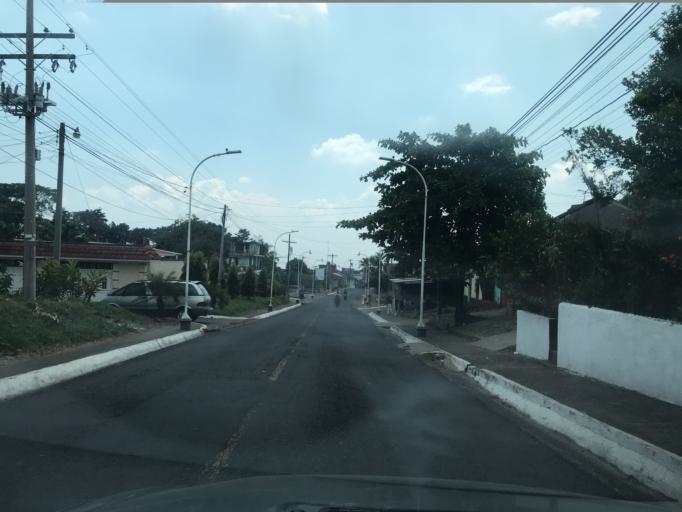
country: GT
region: Suchitepeque
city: San Francisco Zapotitlan
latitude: 14.5923
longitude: -91.5203
